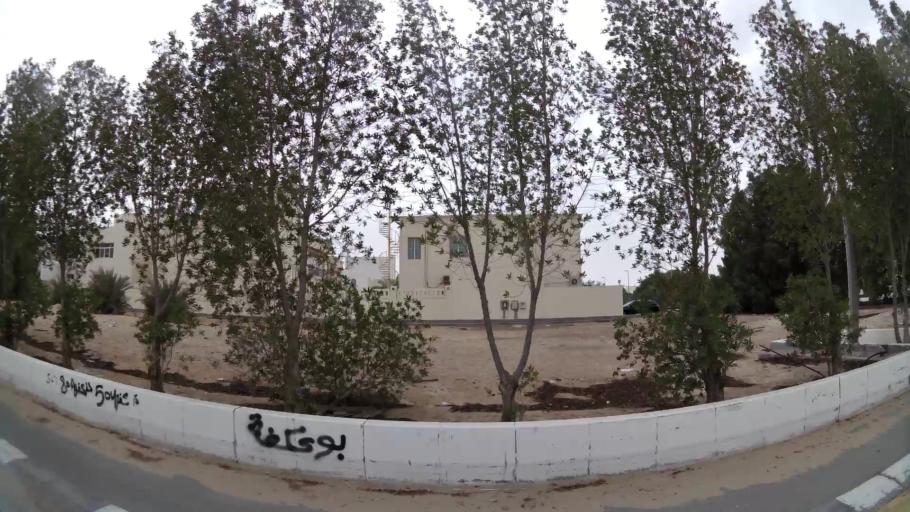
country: AE
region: Abu Dhabi
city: Abu Dhabi
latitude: 24.3757
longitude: 54.6688
